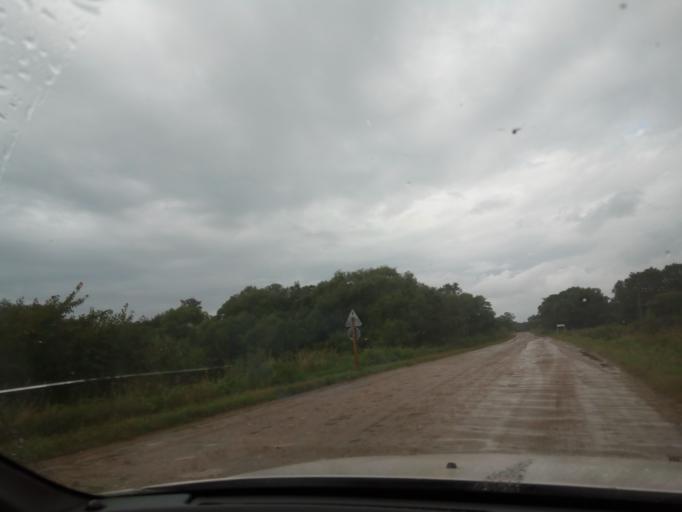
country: RU
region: Primorskiy
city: Lazo
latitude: 45.8536
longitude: 133.6464
